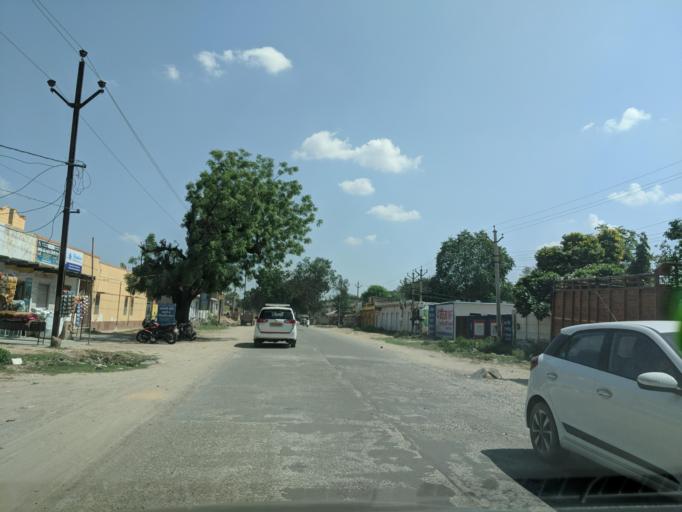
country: IN
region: Rajasthan
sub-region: Jhunjhunun
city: Jhunjhunun
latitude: 28.1370
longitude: 75.3855
